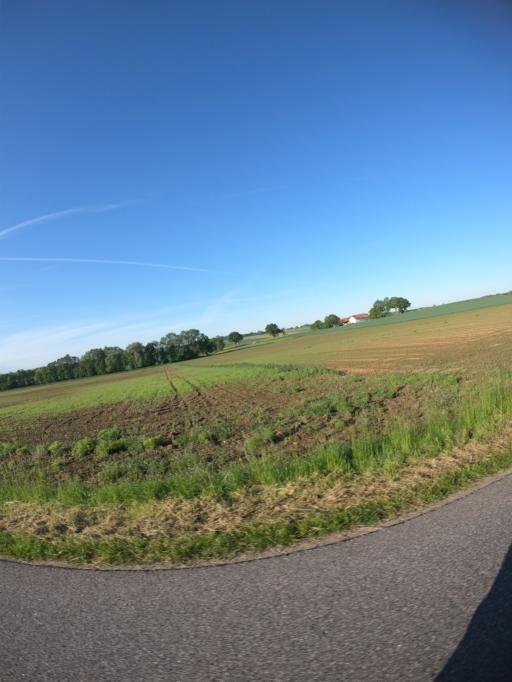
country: DE
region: Bavaria
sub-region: Upper Bavaria
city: Bockhorn
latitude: 48.3092
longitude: 11.9491
